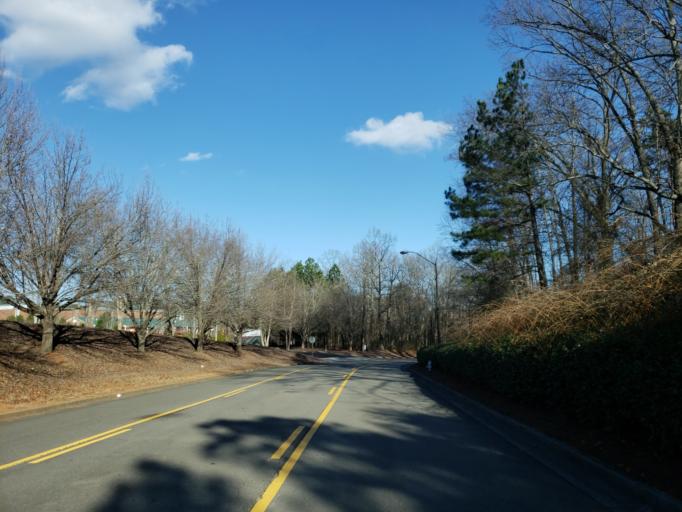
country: US
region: Georgia
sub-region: Cobb County
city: Marietta
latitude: 33.9924
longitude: -84.5256
